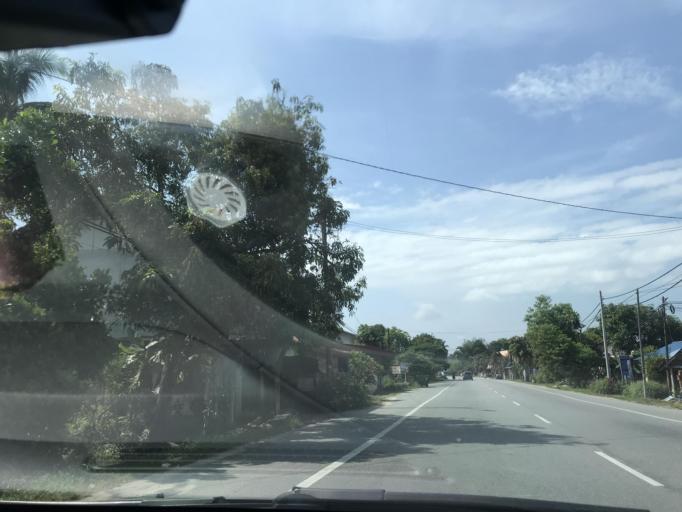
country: MY
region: Kelantan
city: Tumpat
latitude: 6.1413
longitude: 102.1678
